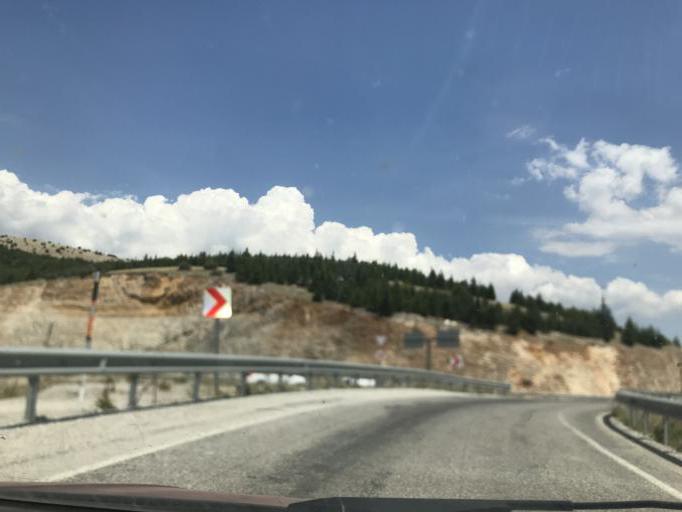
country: TR
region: Denizli
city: Serinhisar
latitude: 37.6286
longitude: 29.2169
